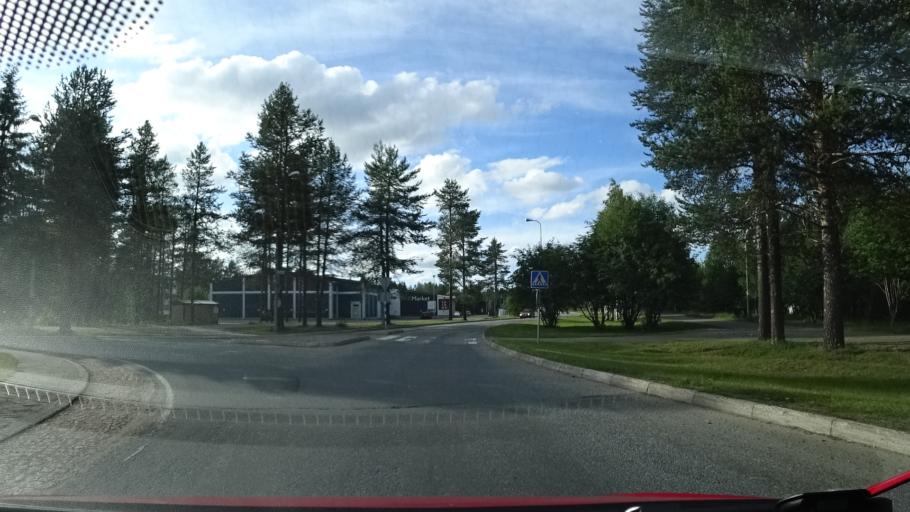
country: FI
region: Lapland
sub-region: Pohjois-Lappi
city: Sodankylae
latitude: 67.4213
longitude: 26.5885
